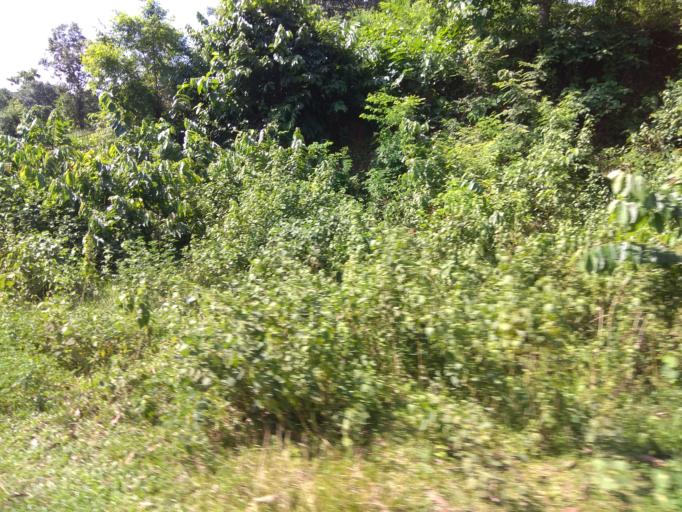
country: BD
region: Chittagong
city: Khagrachhari
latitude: 23.0302
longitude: 92.0128
